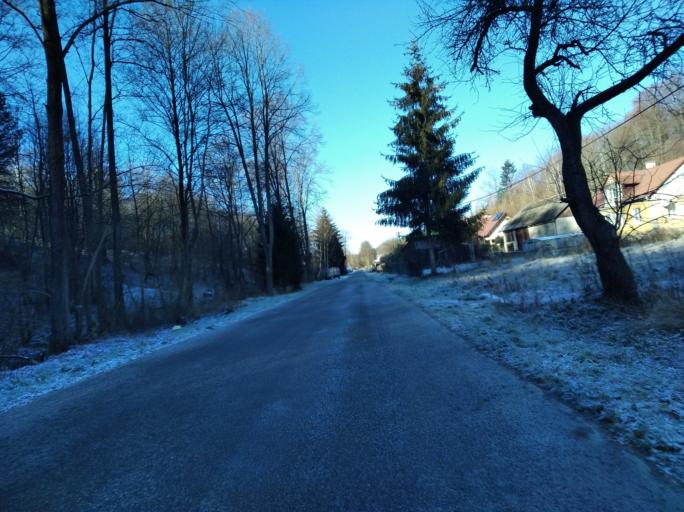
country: PL
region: Subcarpathian Voivodeship
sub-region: Powiat strzyzowski
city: Czudec
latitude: 49.9479
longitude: 21.7826
